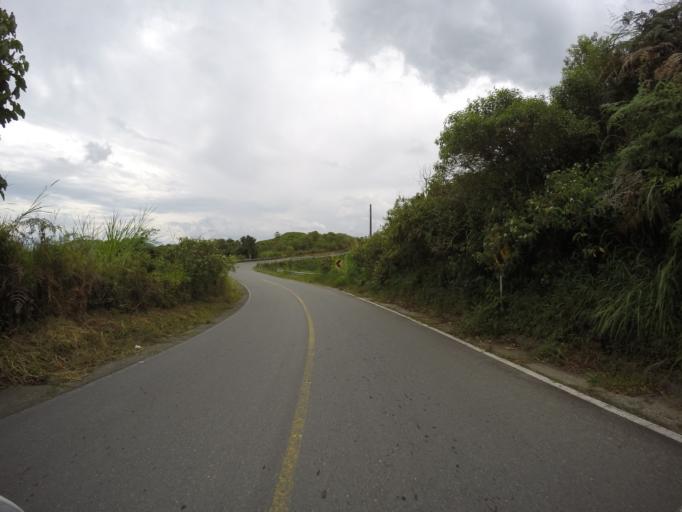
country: CO
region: Quindio
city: Filandia
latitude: 4.6629
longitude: -75.6717
